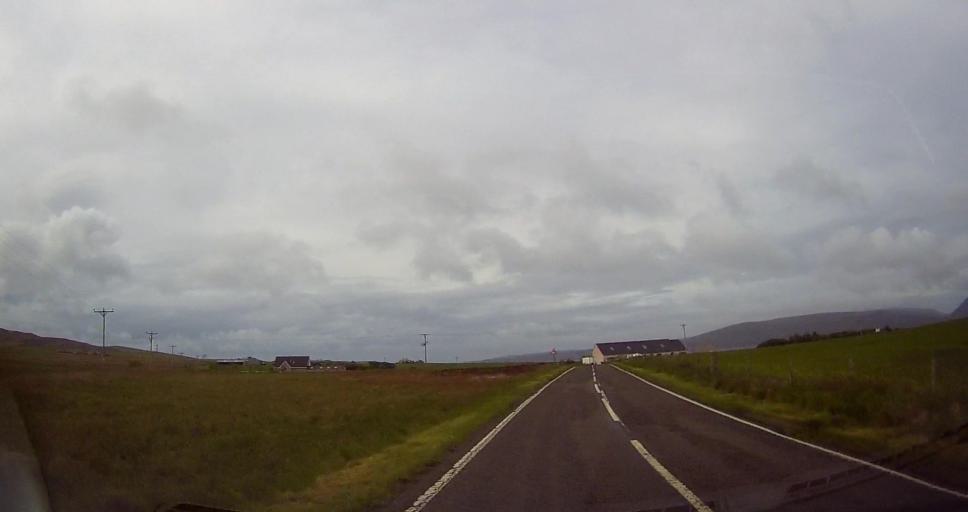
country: GB
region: Scotland
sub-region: Orkney Islands
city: Stromness
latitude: 58.9398
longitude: -3.2128
